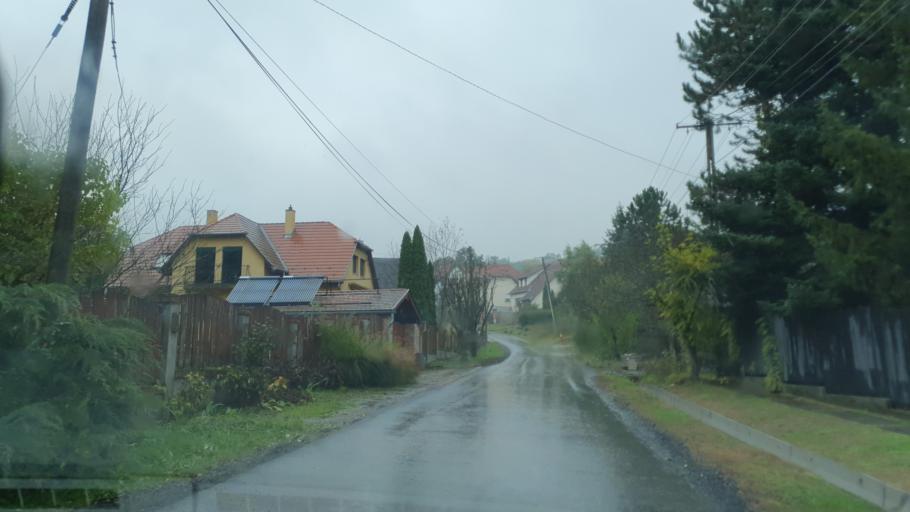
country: HU
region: Pest
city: Veroce
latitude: 47.8464
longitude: 19.0931
